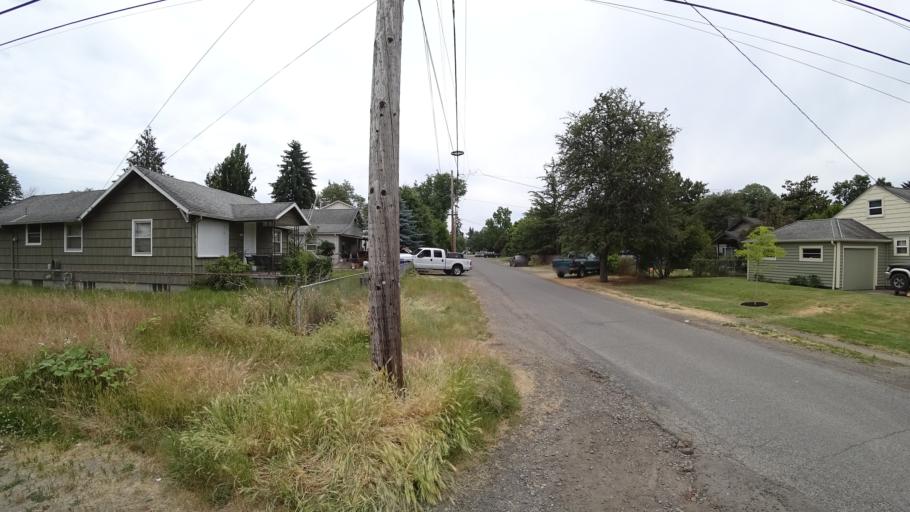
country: US
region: Oregon
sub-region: Multnomah County
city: Lents
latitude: 45.5136
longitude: -122.5731
